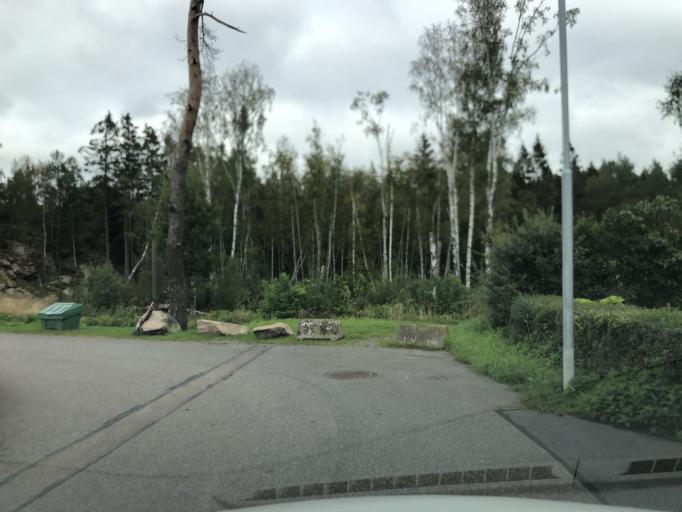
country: SE
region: Vaestra Goetaland
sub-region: Goteborg
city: Majorna
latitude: 57.7443
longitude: 11.9081
